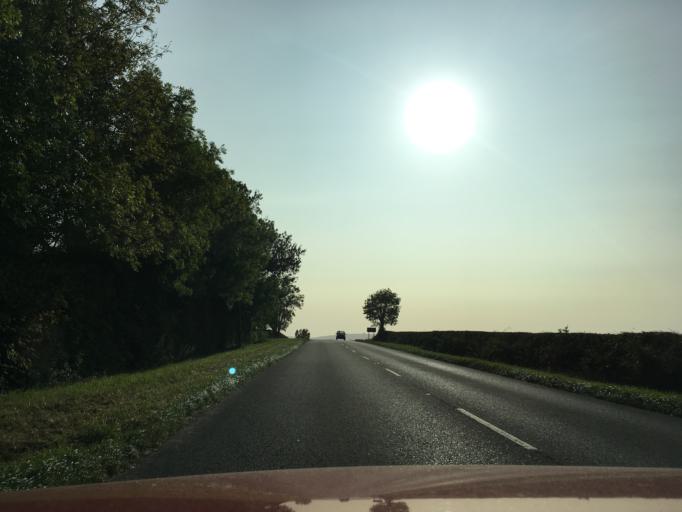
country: GB
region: England
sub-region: Gloucestershire
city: Gloucester
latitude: 51.9607
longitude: -2.2774
